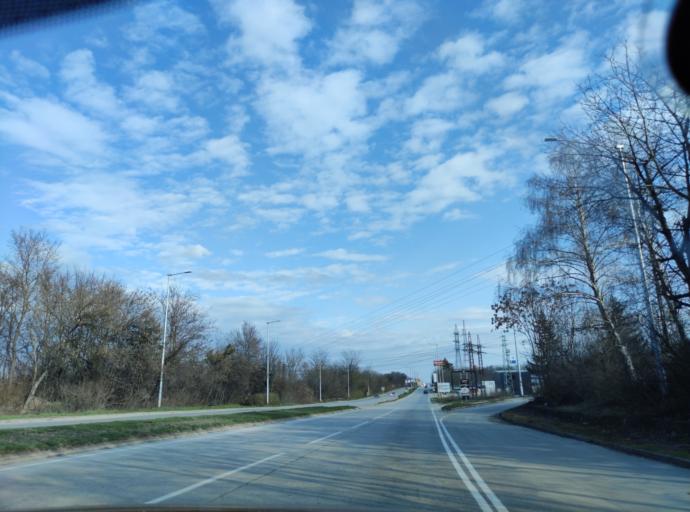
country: BG
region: Pleven
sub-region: Obshtina Pleven
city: Pleven
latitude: 43.4343
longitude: 24.5734
